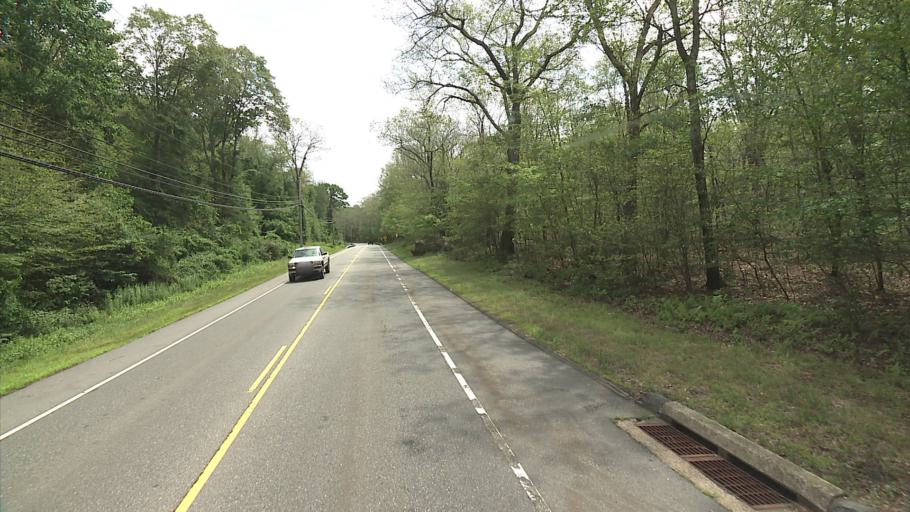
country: US
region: Connecticut
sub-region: New Haven County
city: Madison
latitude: 41.3613
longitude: -72.5802
